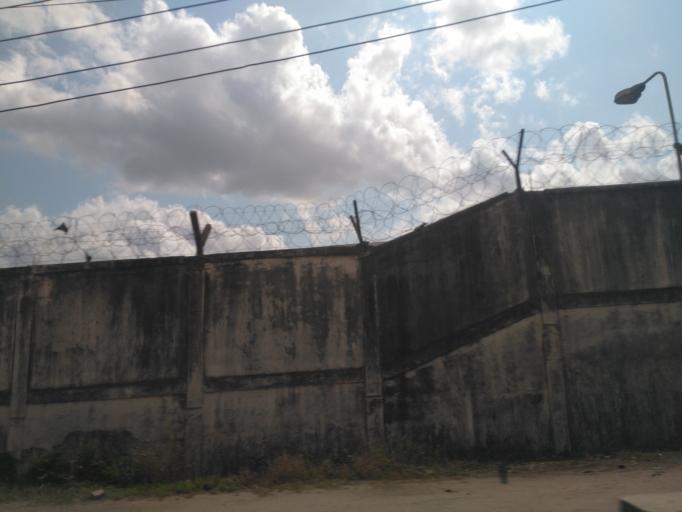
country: TZ
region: Dar es Salaam
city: Dar es Salaam
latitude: -6.8348
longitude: 39.2903
